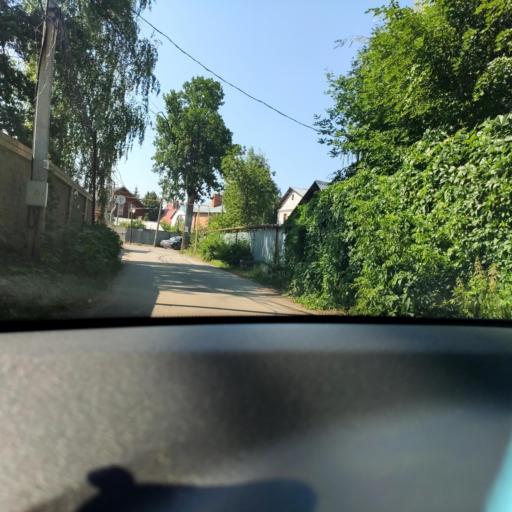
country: RU
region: Samara
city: Samara
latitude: 53.2858
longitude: 50.1955
